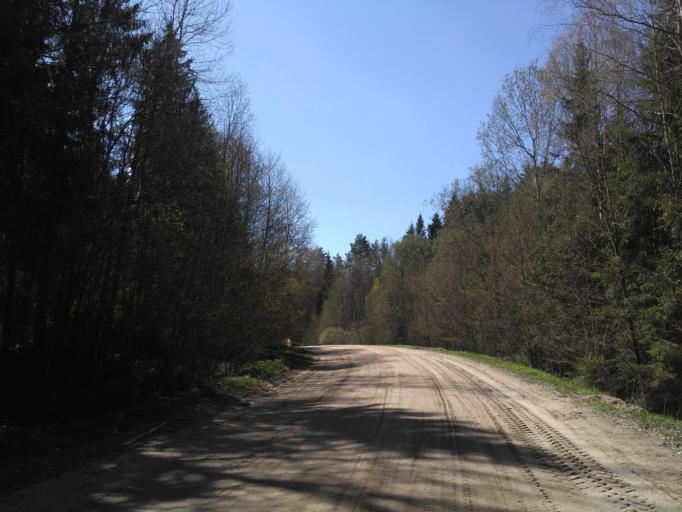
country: BY
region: Minsk
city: Loshnitsa
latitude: 54.3121
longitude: 28.6425
